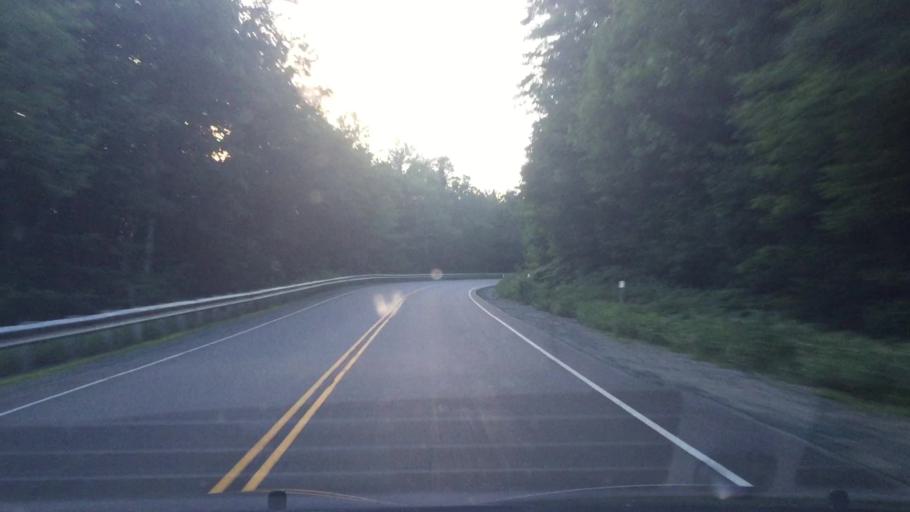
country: US
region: New Hampshire
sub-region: Grafton County
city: Woodstock
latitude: 44.0343
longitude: -71.5189
